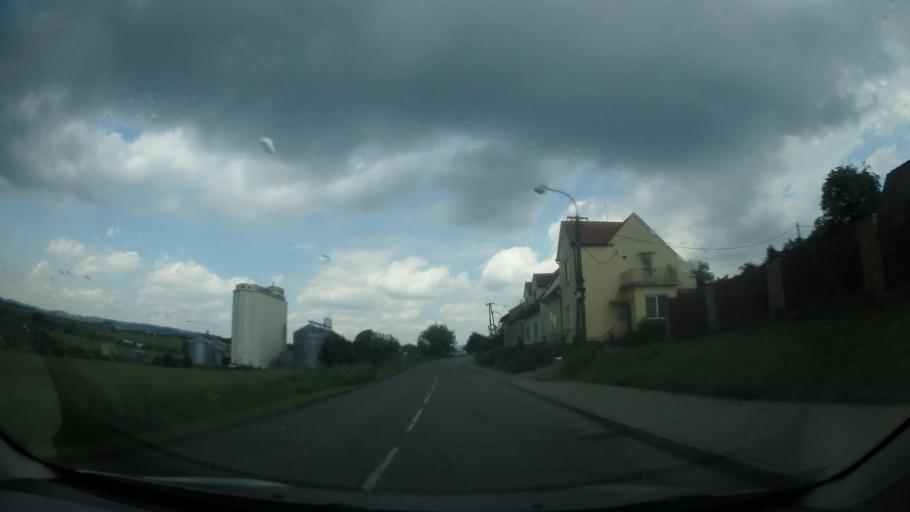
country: CZ
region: South Moravian
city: Svitavka
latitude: 49.4784
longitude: 16.6000
